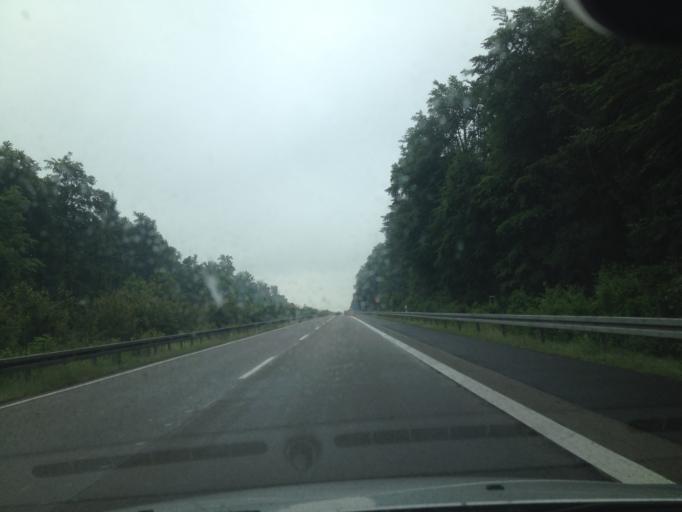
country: DE
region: Hesse
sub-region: Regierungsbezirk Darmstadt
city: Munzenberg
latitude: 50.4334
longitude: 8.8003
